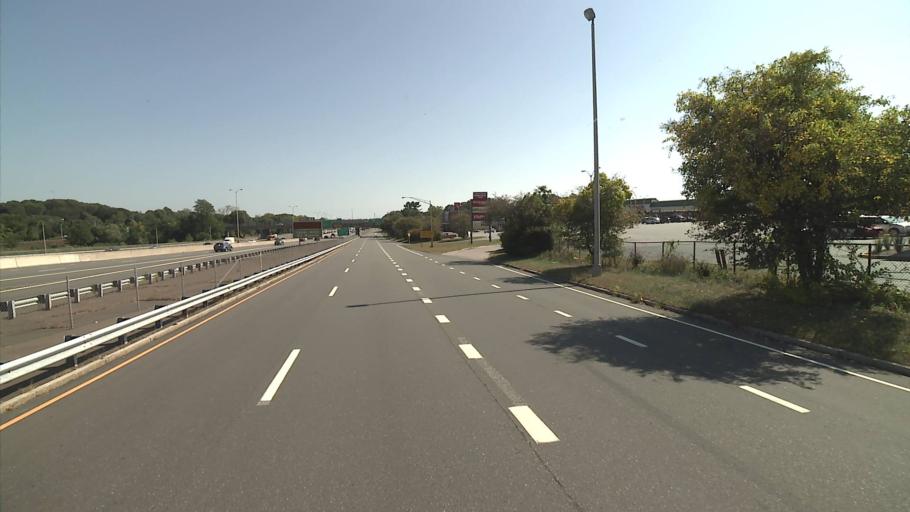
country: US
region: Connecticut
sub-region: New London County
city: New London
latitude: 41.3694
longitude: -72.1188
